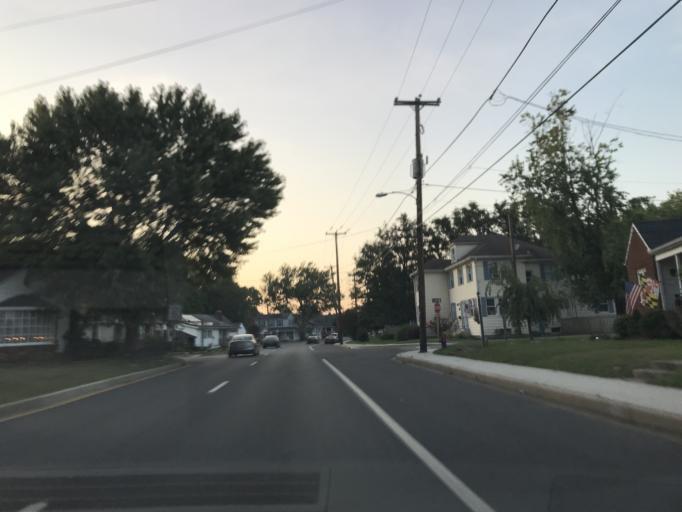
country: US
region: Maryland
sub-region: Cecil County
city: North East
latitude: 39.5982
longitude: -75.9406
